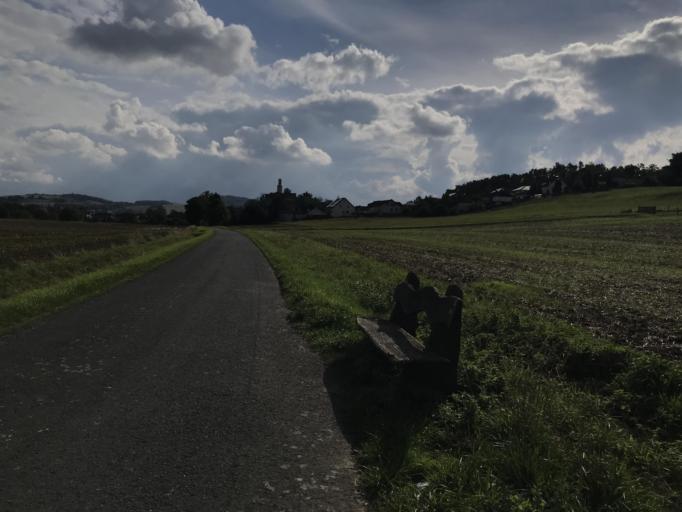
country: DE
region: Hesse
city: Felsberg
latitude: 51.1448
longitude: 9.4193
